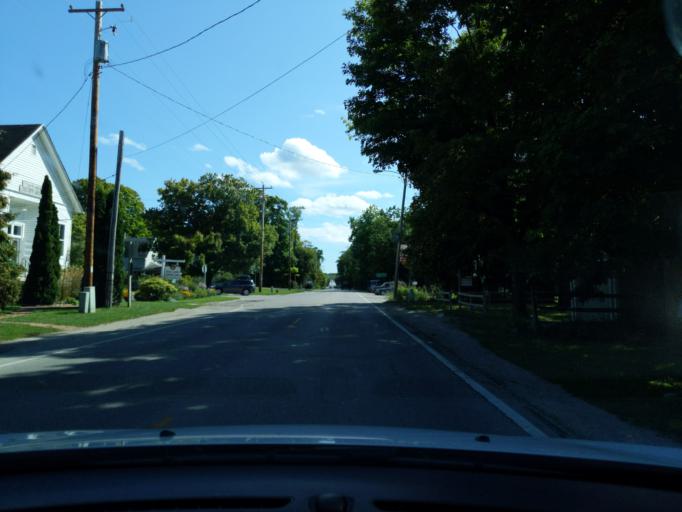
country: US
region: Wisconsin
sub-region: Door County
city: Sturgeon Bay
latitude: 45.2008
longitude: -87.1189
